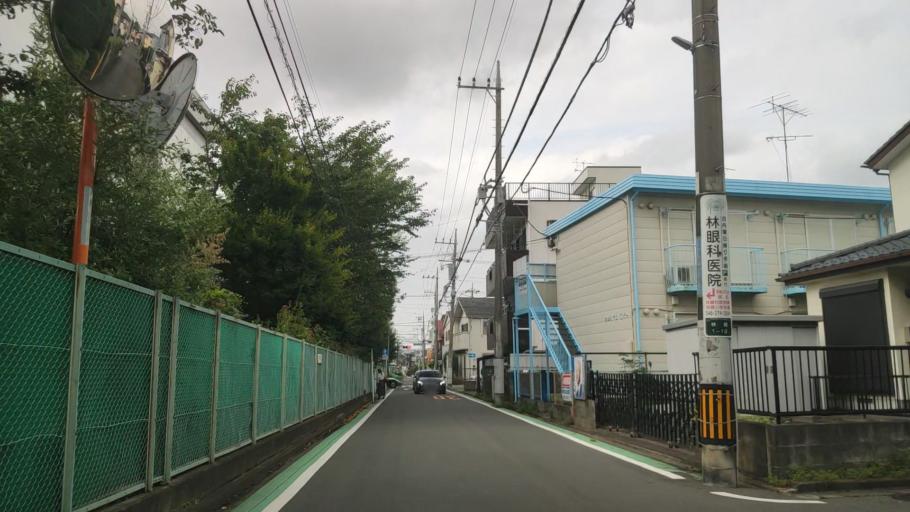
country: JP
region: Kanagawa
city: Minami-rinkan
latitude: 35.4967
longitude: 139.4504
